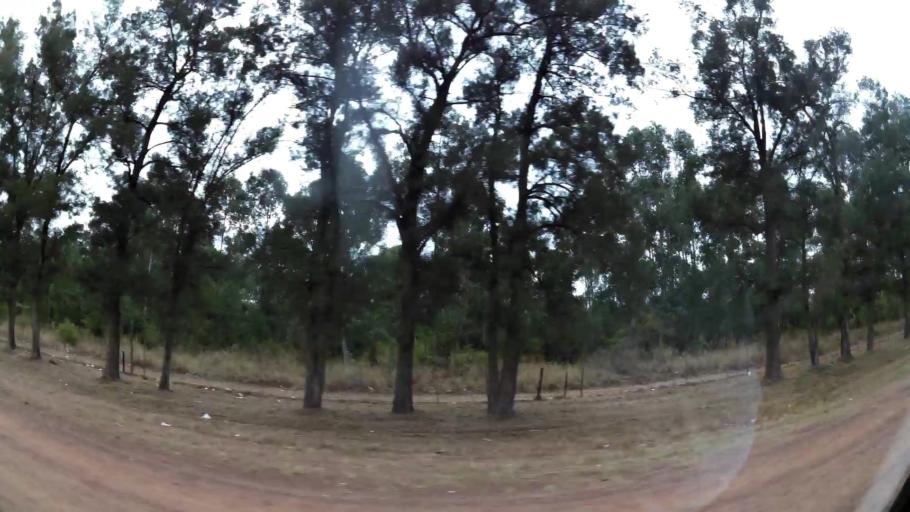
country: ZA
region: Limpopo
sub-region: Waterberg District Municipality
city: Modimolle
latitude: -24.6763
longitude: 28.4421
